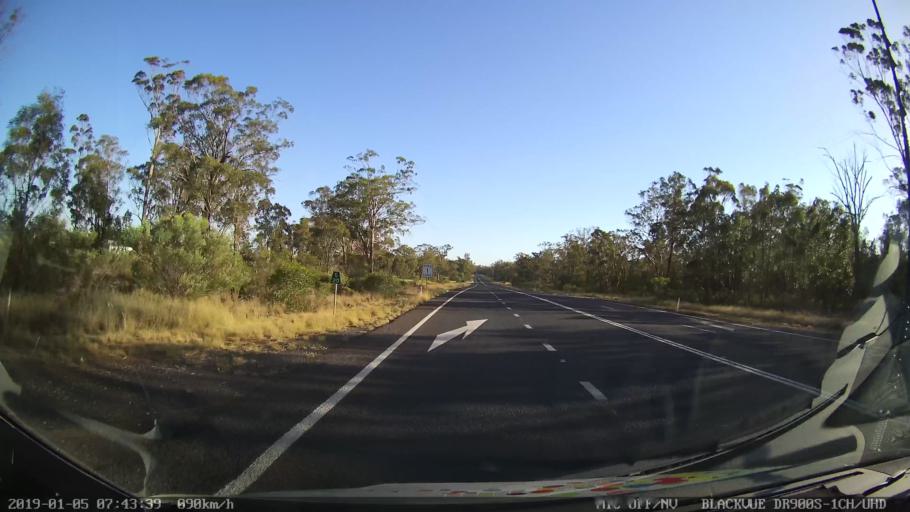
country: AU
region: New South Wales
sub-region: Gilgandra
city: Gilgandra
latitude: -31.8825
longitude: 148.6352
